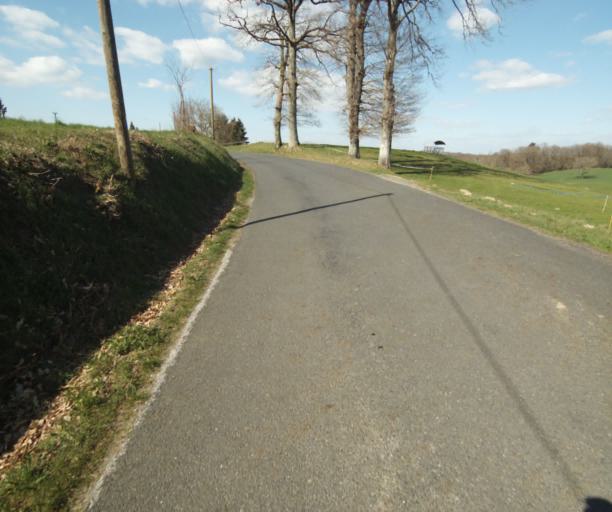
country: FR
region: Limousin
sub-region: Departement de la Correze
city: Saint-Mexant
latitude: 45.2924
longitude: 1.6512
